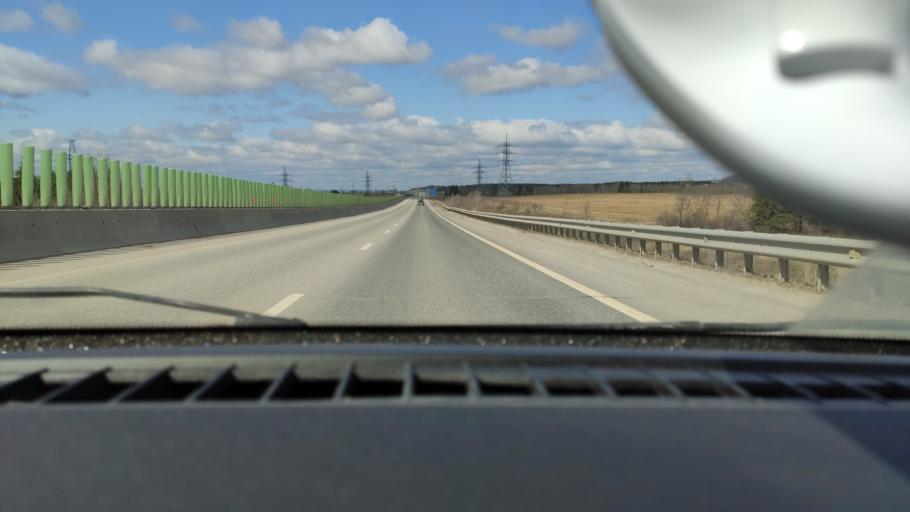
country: RU
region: Perm
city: Froly
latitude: 57.9312
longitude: 56.2865
